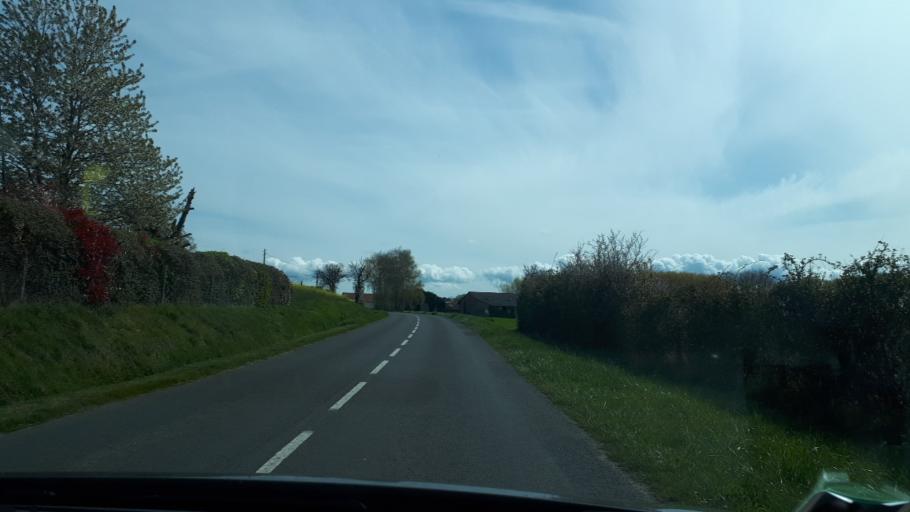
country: FR
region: Pays de la Loire
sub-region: Departement de la Sarthe
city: Yvre-le-Polin
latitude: 47.8232
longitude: 0.1663
